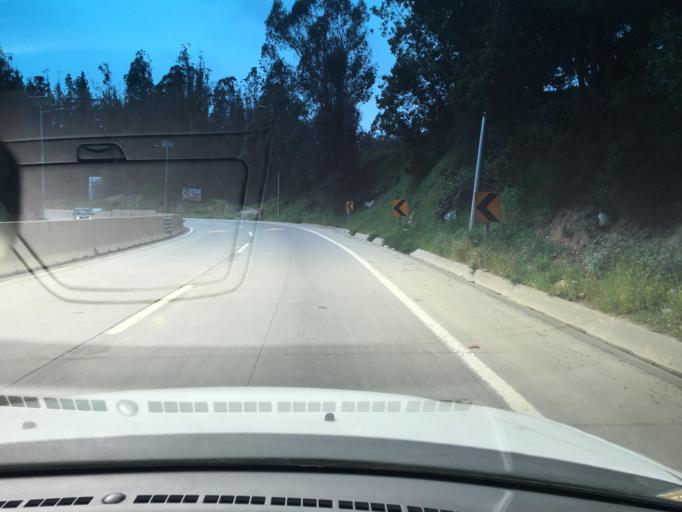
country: CL
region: Valparaiso
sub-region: Provincia de Valparaiso
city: Vina del Mar
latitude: -33.0999
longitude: -71.5727
